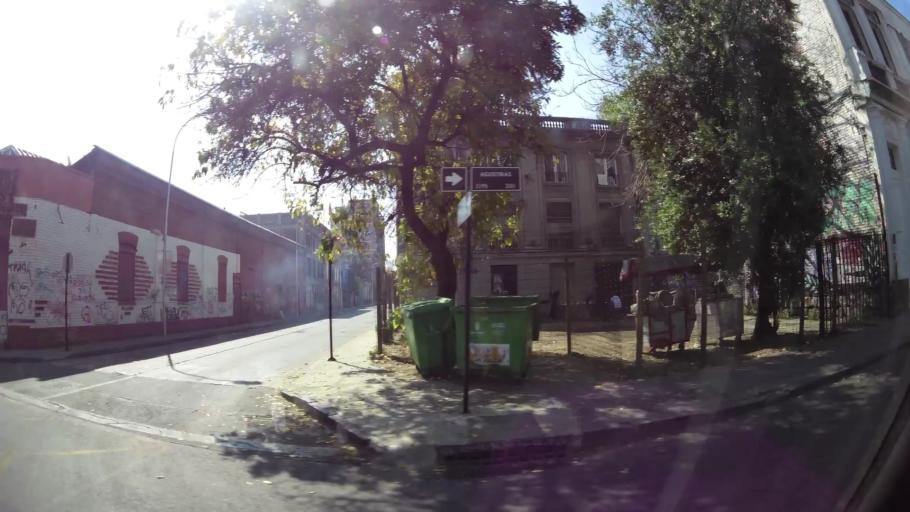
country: CL
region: Santiago Metropolitan
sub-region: Provincia de Santiago
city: Santiago
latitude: -33.4423
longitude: -70.6663
